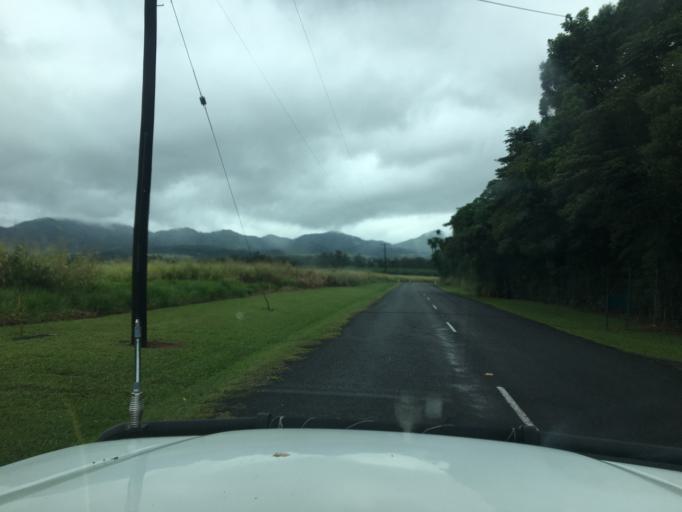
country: AU
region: Queensland
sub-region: Cassowary Coast
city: Innisfail
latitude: -17.4396
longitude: 145.8605
